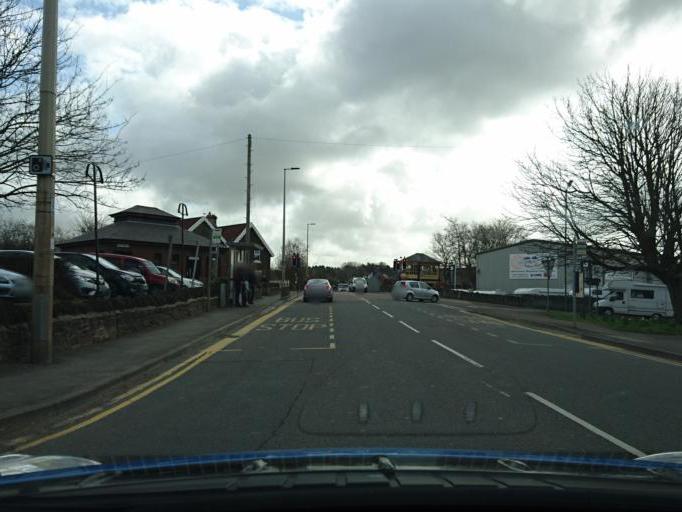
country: GB
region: England
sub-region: South Gloucestershire
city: Siston
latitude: 51.4599
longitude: -2.4756
